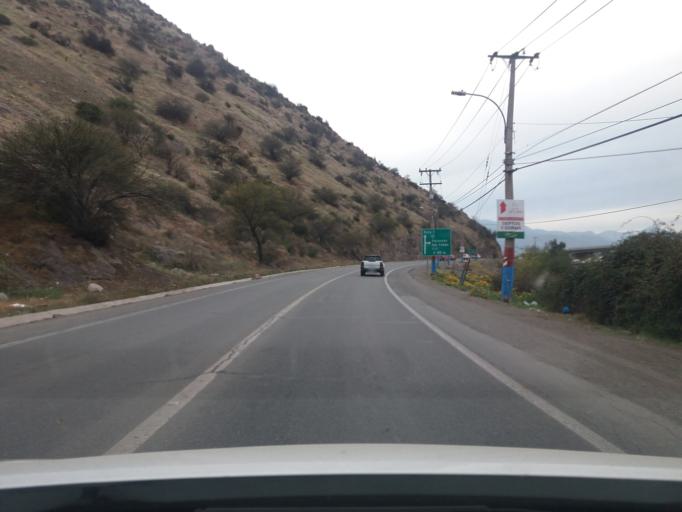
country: CL
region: Valparaiso
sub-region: Provincia de San Felipe
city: San Felipe
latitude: -32.7606
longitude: -70.7360
